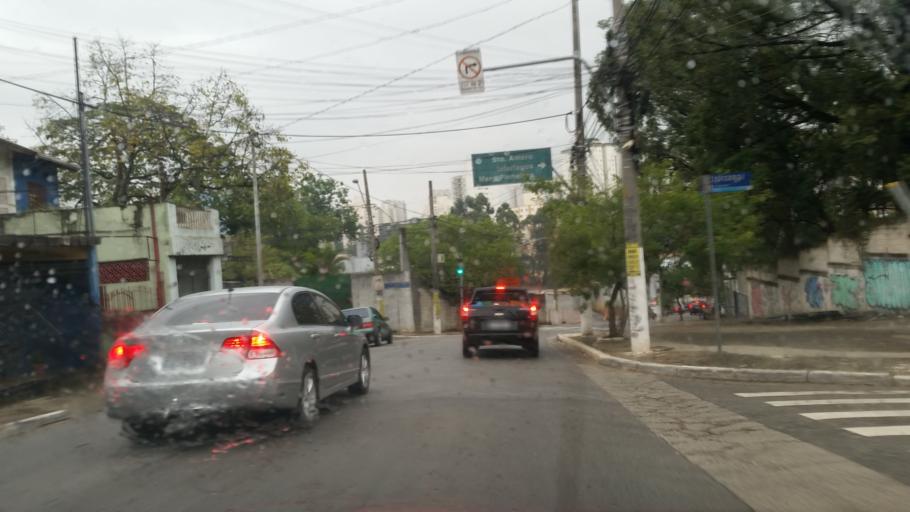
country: BR
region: Sao Paulo
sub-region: Diadema
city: Diadema
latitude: -23.6366
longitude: -46.6613
